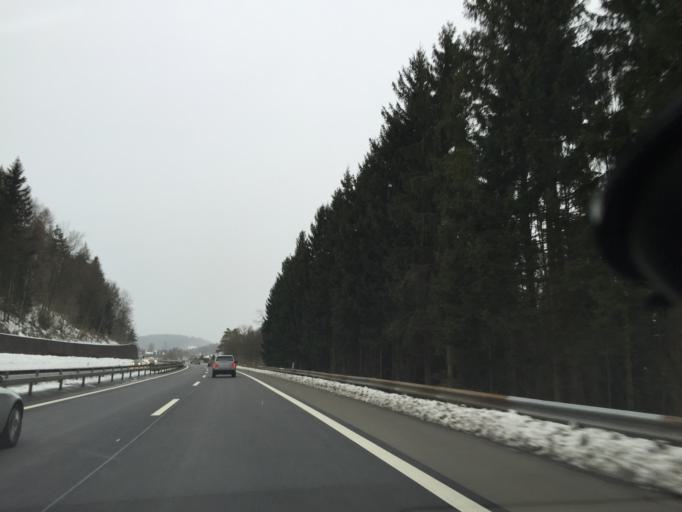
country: CH
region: Zurich
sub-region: Bezirk Horgen
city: Thalwil / Sued
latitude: 47.2824
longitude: 8.5600
